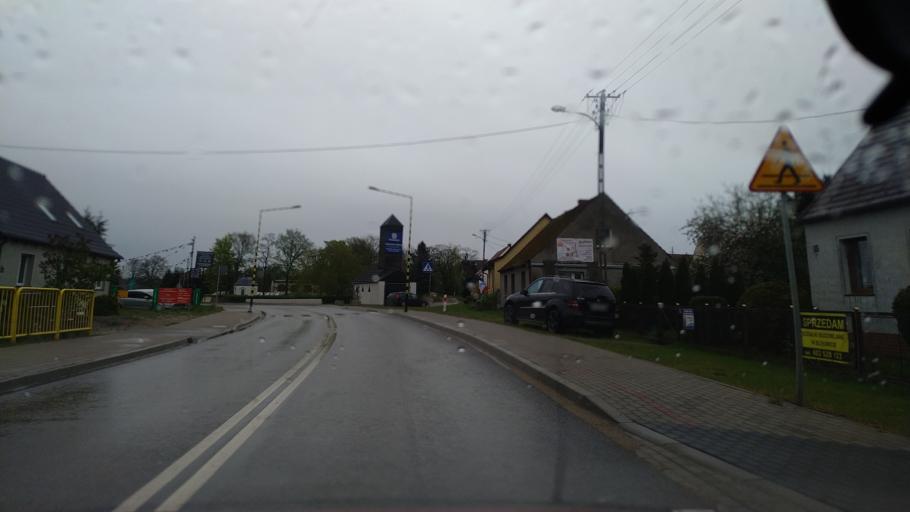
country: PL
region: Greater Poland Voivodeship
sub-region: Powiat zlotowski
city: Zlotow
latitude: 53.3475
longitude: 17.0231
